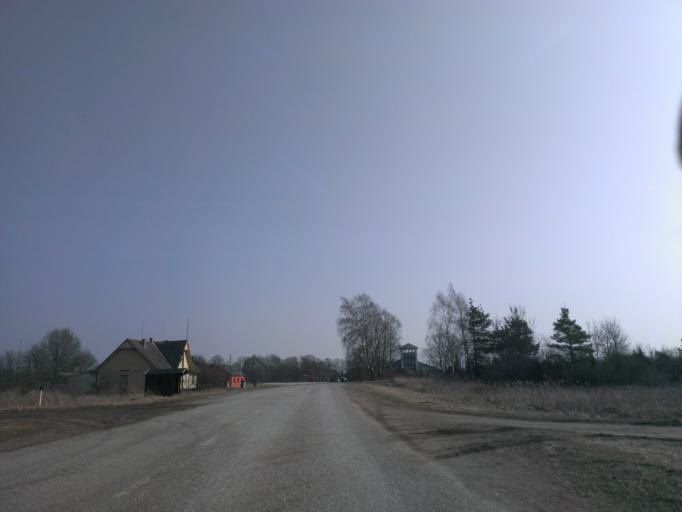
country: EE
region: Saare
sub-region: Kuressaare linn
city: Kuressaare
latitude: 58.3021
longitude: 22.7051
